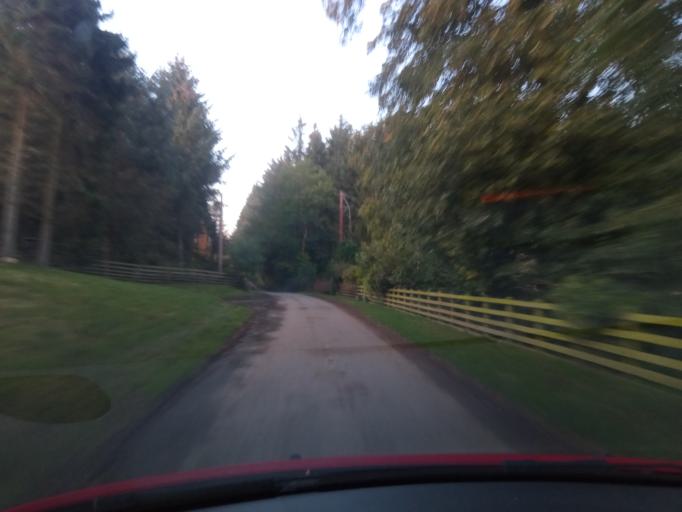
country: GB
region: Scotland
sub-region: Fife
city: Pathhead
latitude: 55.7956
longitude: -2.8893
